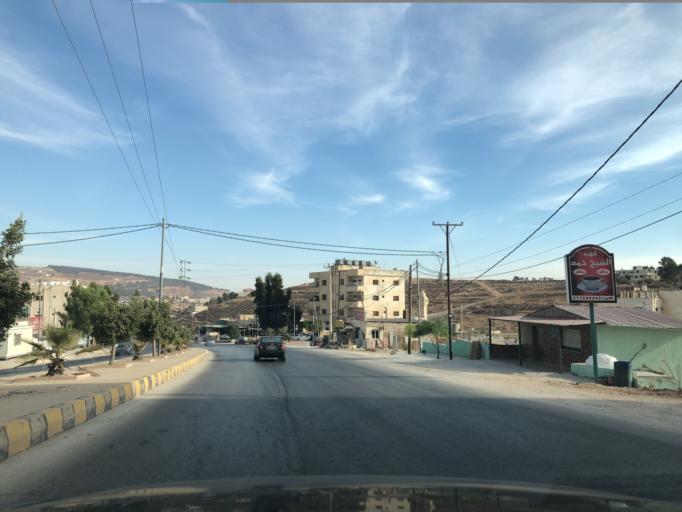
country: JO
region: Jerash
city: Jarash
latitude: 32.2724
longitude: 35.8804
